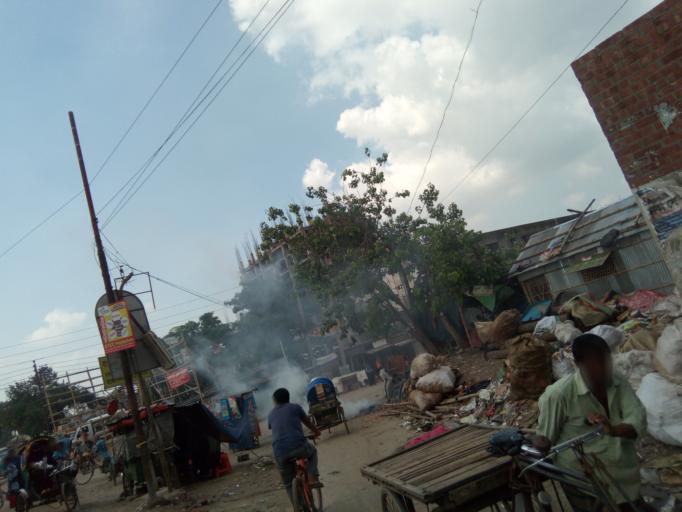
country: BD
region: Dhaka
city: Azimpur
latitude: 23.7445
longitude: 90.3596
